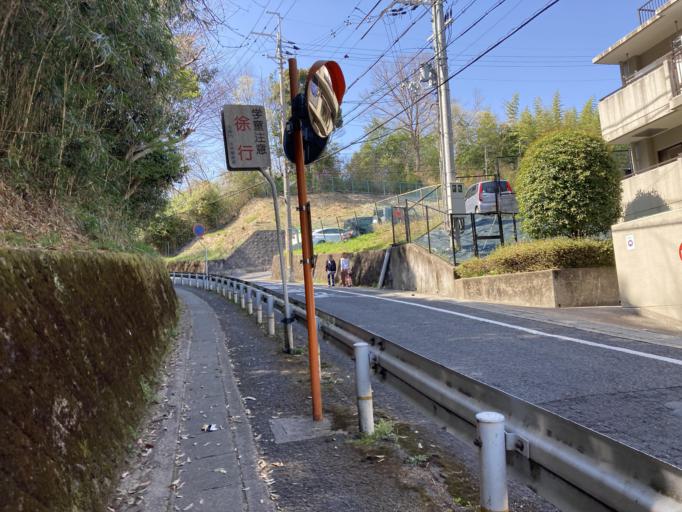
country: JP
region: Nara
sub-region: Ikoma-shi
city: Ikoma
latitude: 34.7040
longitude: 135.6905
